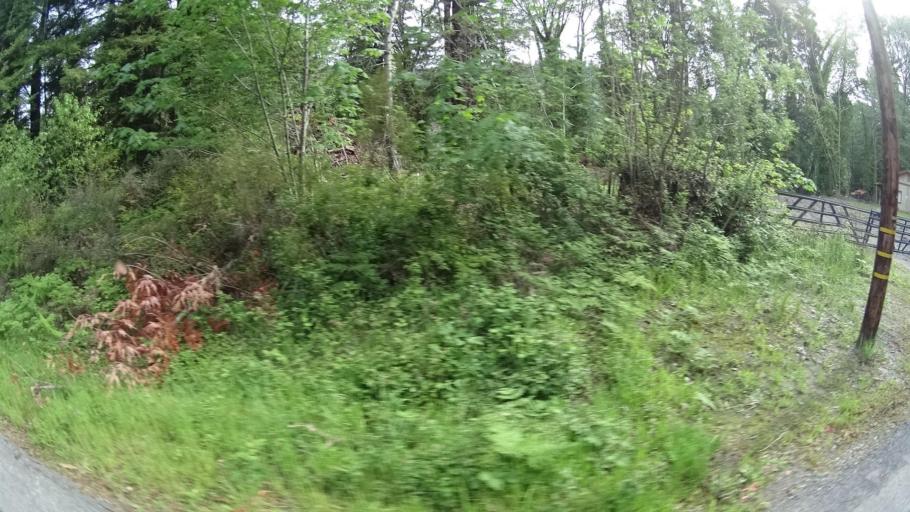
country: US
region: California
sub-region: Humboldt County
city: Redway
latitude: 40.3425
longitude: -123.8815
